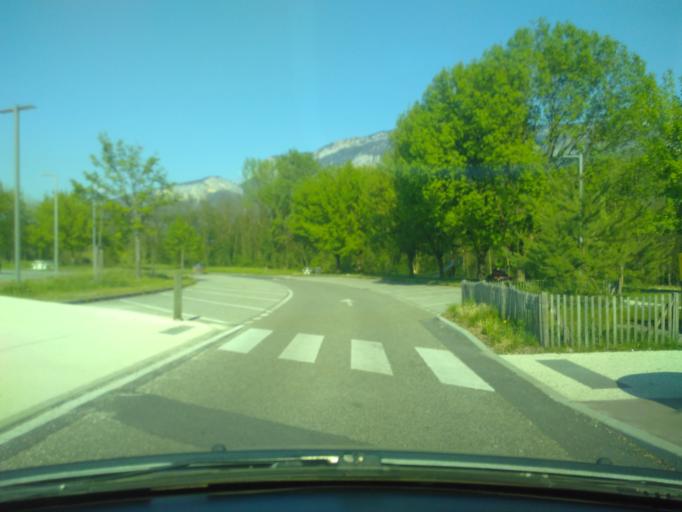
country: FR
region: Rhone-Alpes
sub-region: Departement de l'Isere
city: Vinay
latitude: 45.2071
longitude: 5.4551
